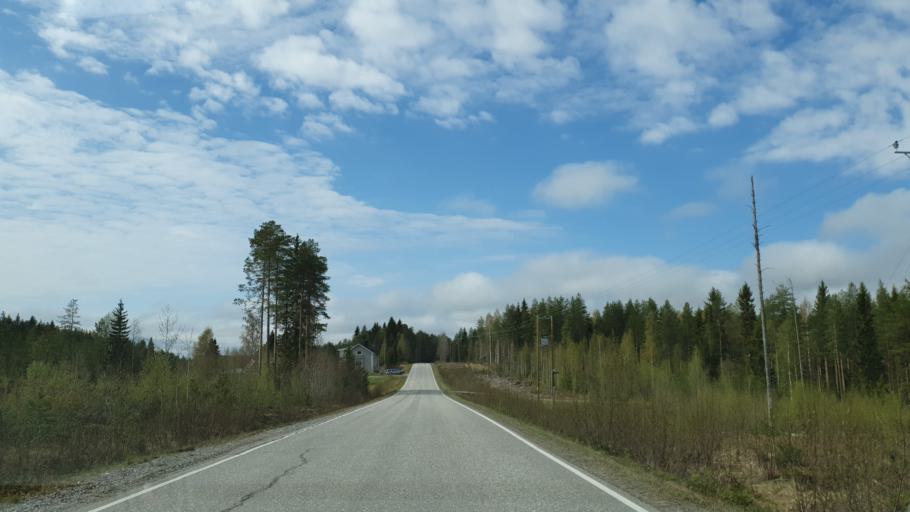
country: FI
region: Kainuu
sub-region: Kehys-Kainuu
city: Kuhmo
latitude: 64.1221
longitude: 29.6642
